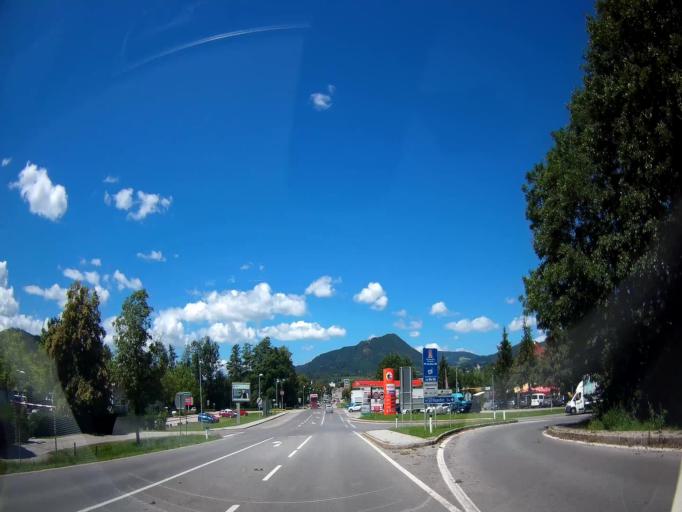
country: AT
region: Carinthia
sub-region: Politischer Bezirk Sankt Veit an der Glan
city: Sankt Veit an der Glan
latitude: 46.7660
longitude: 14.3785
